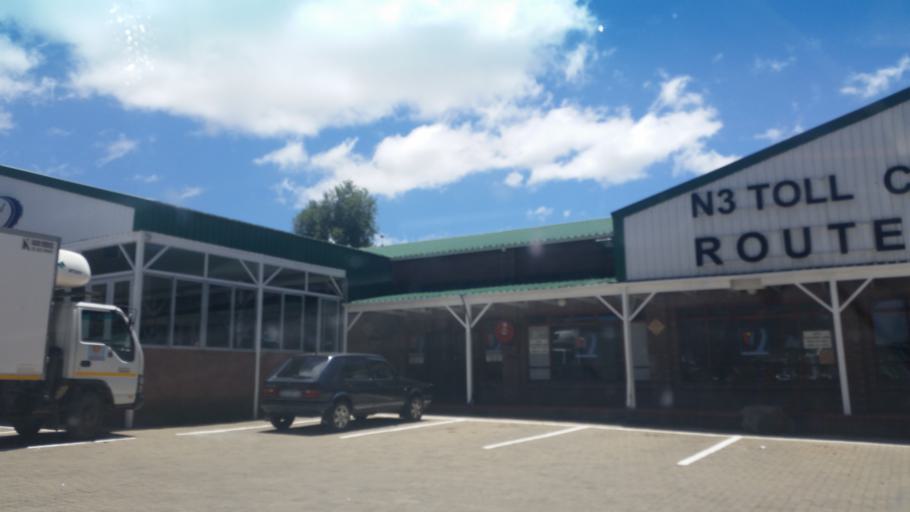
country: ZA
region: Orange Free State
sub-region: Thabo Mofutsanyana District Municipality
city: Harrismith
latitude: -28.2556
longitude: 29.1165
